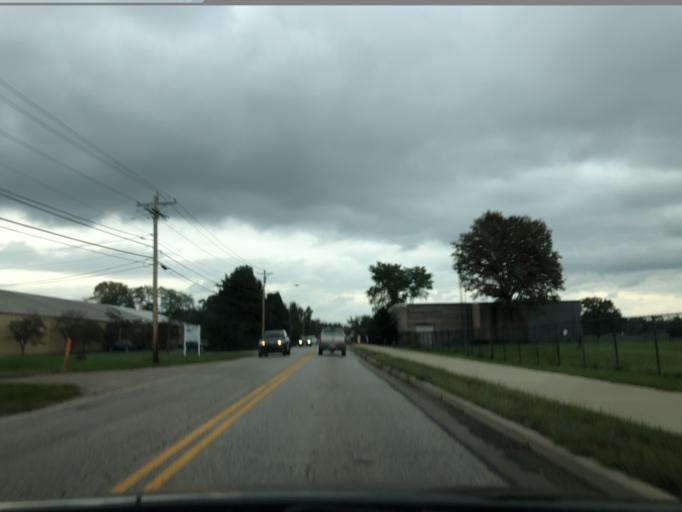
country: US
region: Ohio
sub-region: Hamilton County
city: Turpin Hills
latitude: 39.1117
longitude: -84.4194
